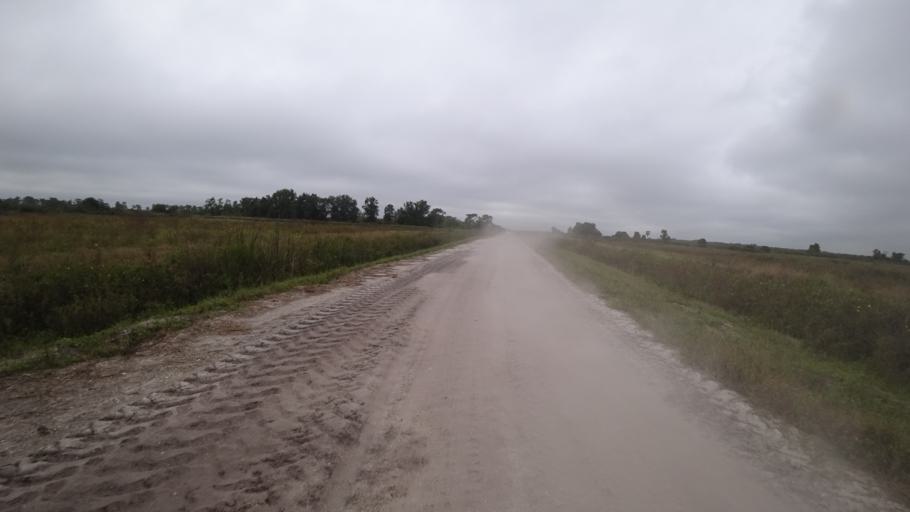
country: US
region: Florida
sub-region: Sarasota County
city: Warm Mineral Springs
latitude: 27.2940
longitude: -82.1346
